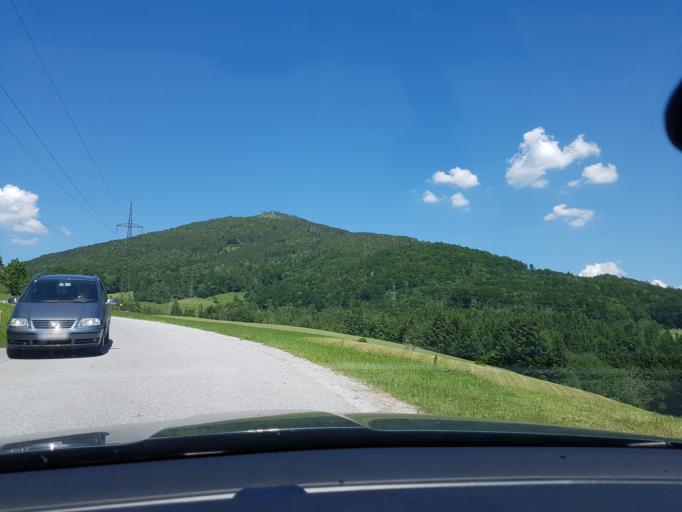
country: AT
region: Salzburg
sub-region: Politischer Bezirk Salzburg-Umgebung
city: Elsbethen
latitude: 47.7780
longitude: 13.1187
